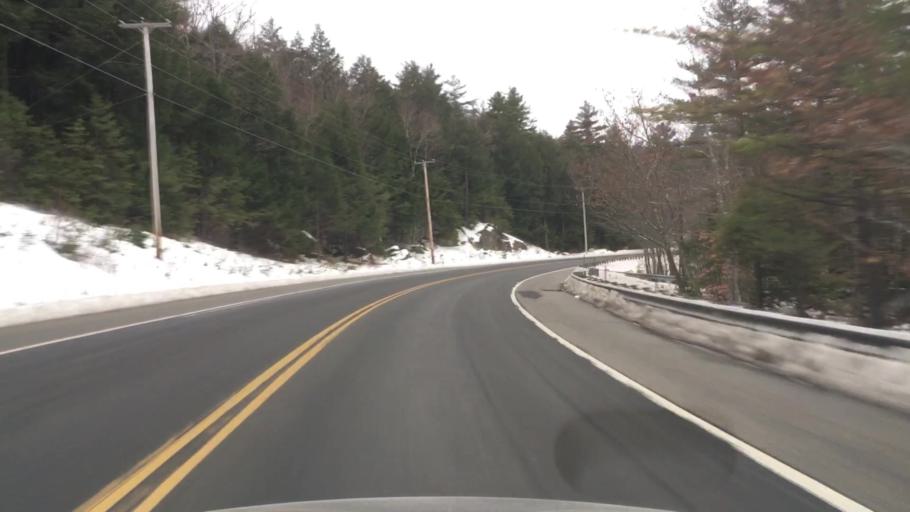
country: US
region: New Hampshire
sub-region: Merrimack County
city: Henniker
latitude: 43.2173
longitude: -71.8776
